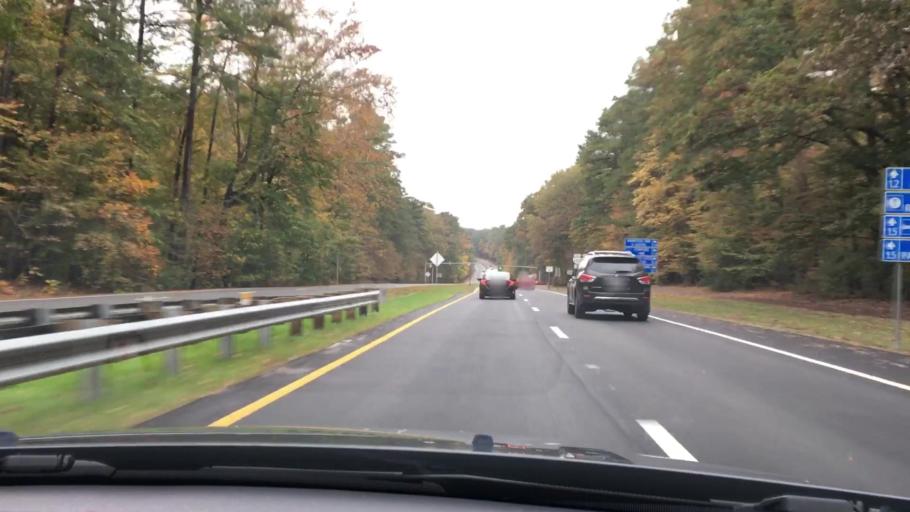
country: US
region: Virginia
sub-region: City of Williamsburg
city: Williamsburg
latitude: 37.2986
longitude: -76.6858
